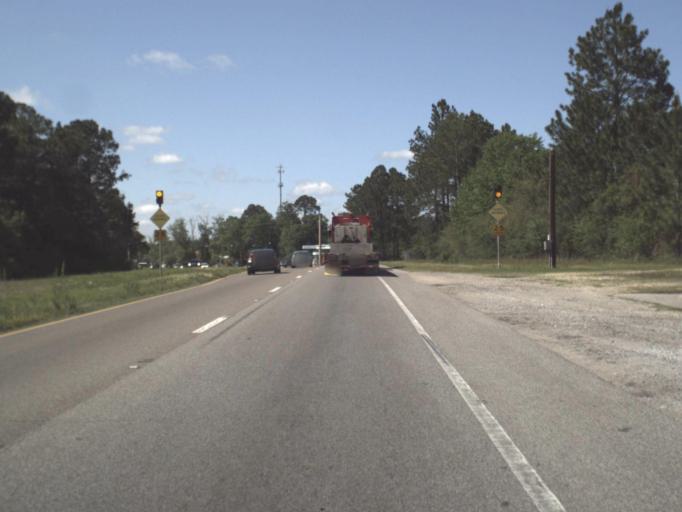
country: US
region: Florida
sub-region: Escambia County
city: Gonzalez
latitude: 30.5740
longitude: -87.2920
